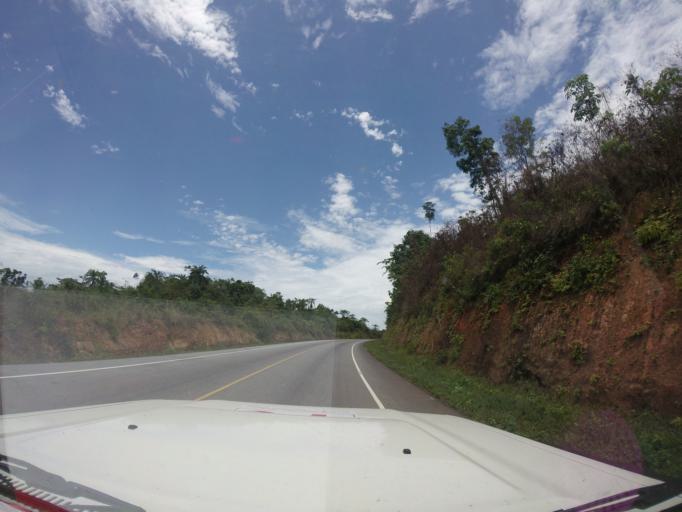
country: LR
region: Bong
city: Gbarnga
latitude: 6.8256
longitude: -9.8702
